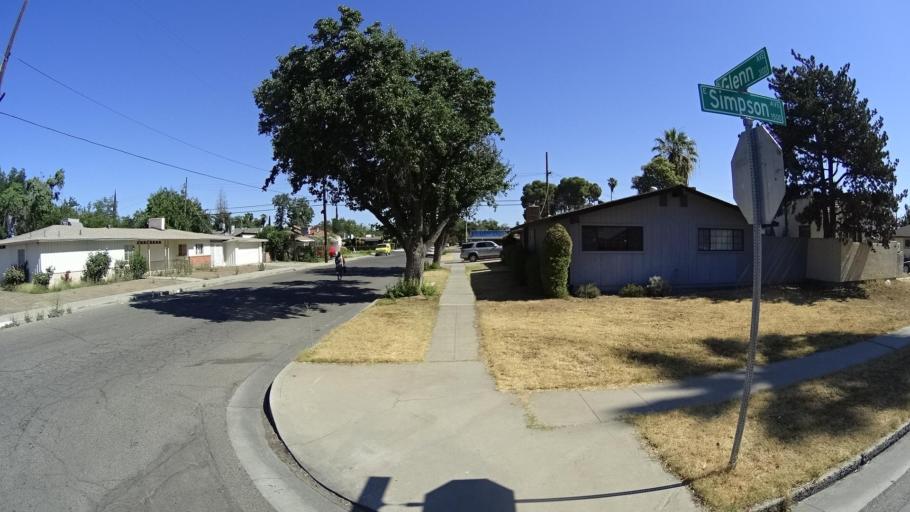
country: US
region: California
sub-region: Fresno County
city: Fresno
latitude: 36.7786
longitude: -119.7927
